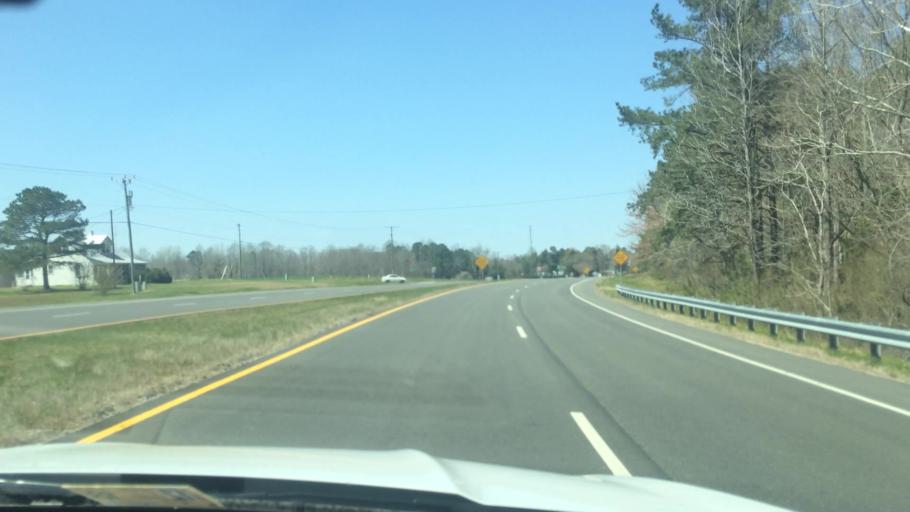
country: US
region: Virginia
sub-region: Middlesex County
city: Saluda
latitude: 37.6002
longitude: -76.5843
